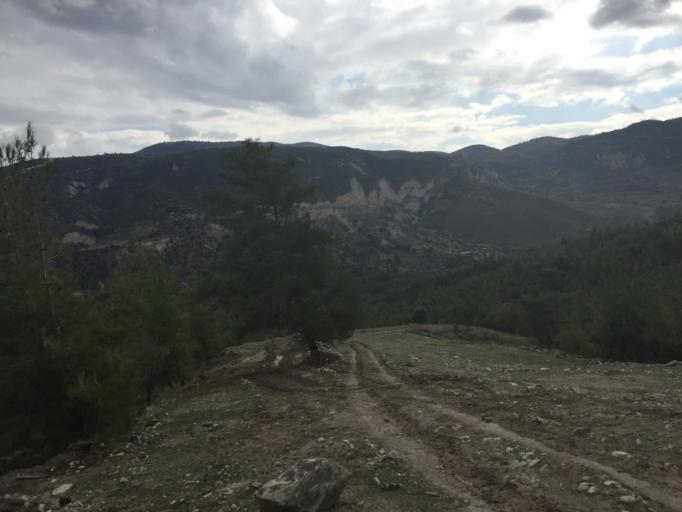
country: CY
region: Limassol
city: Pachna
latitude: 34.8861
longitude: 32.6688
